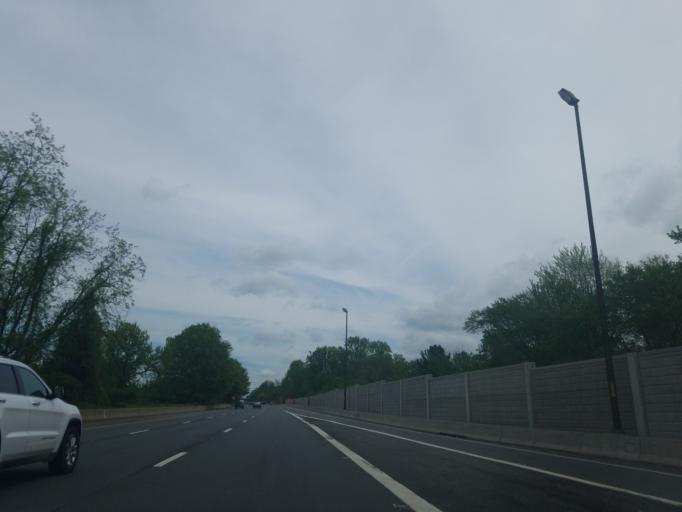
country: US
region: Virginia
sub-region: Fairfax County
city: Dunn Loring
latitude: 38.8865
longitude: -77.2185
